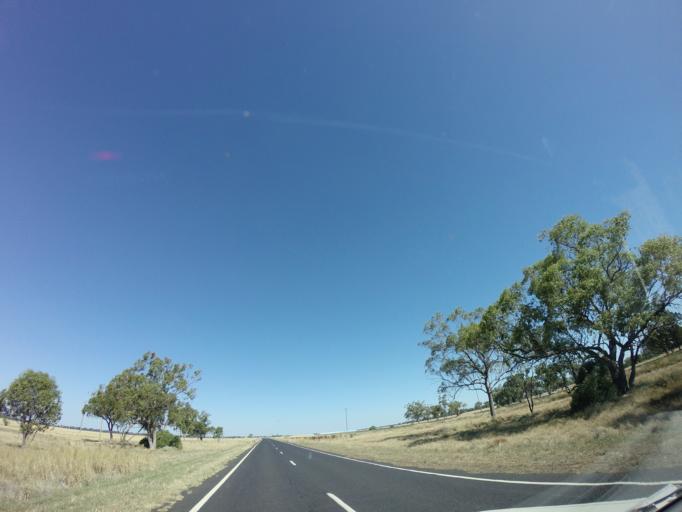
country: AU
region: New South Wales
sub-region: Bogan
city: Nyngan
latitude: -31.8262
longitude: 147.6955
